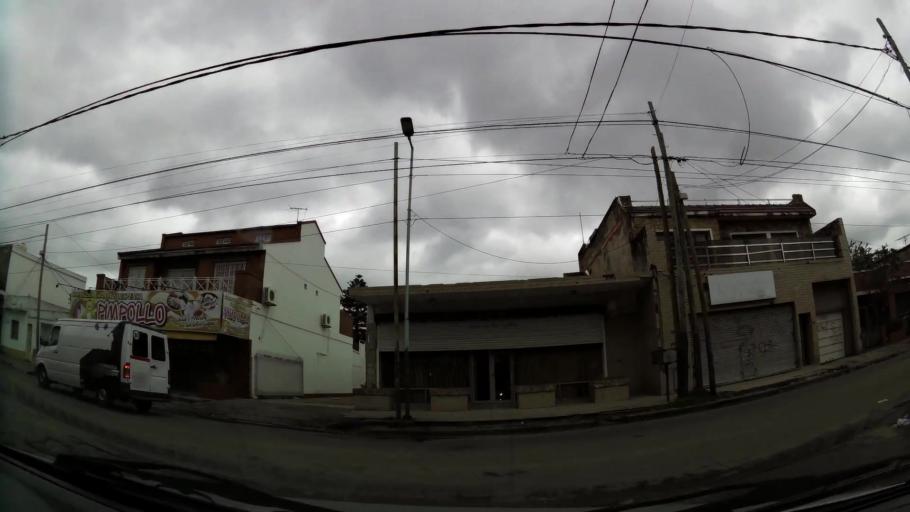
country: AR
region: Buenos Aires
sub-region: Partido de Lomas de Zamora
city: Lomas de Zamora
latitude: -34.7524
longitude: -58.3695
